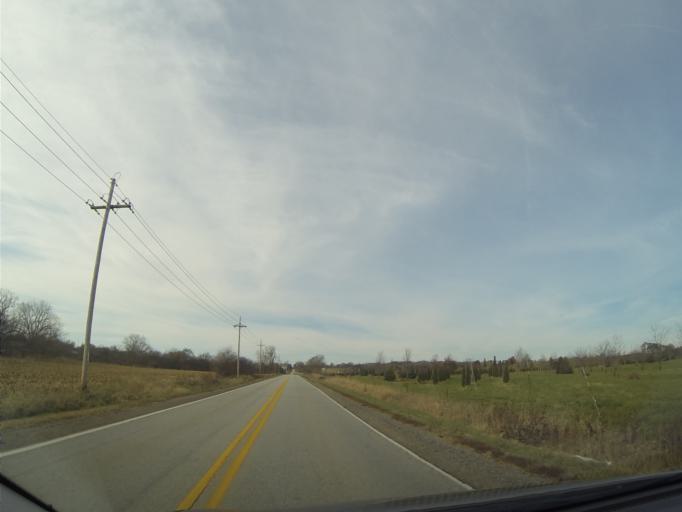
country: US
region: Nebraska
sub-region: Douglas County
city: Elkhorn
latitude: 41.2776
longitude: -96.1973
